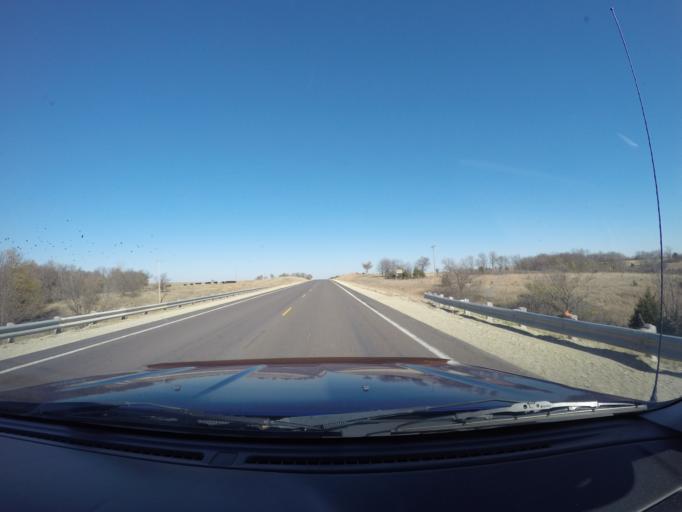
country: US
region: Kansas
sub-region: Marshall County
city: Blue Rapids
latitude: 39.6671
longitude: -96.7505
